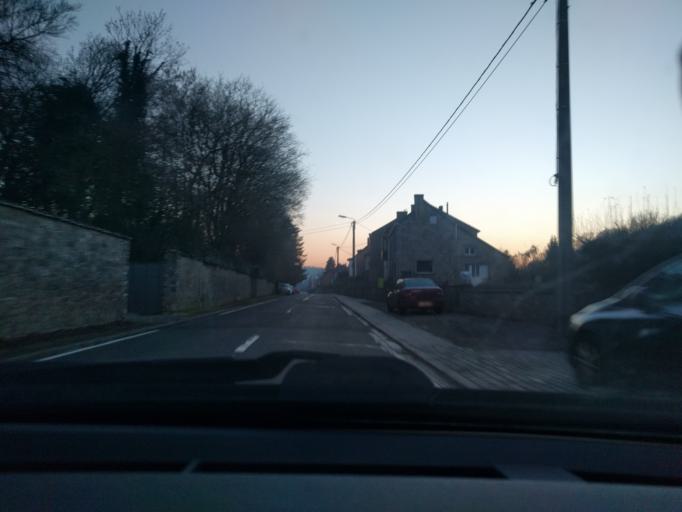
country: BE
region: Wallonia
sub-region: Province de Namur
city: Namur
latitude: 50.4757
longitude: 4.9328
